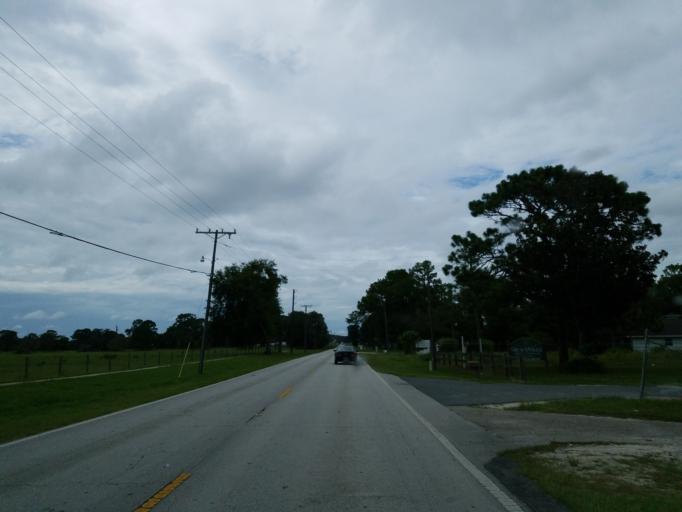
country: US
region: Florida
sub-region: Sumter County
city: Lake Panasoffkee
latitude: 28.7789
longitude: -82.1254
